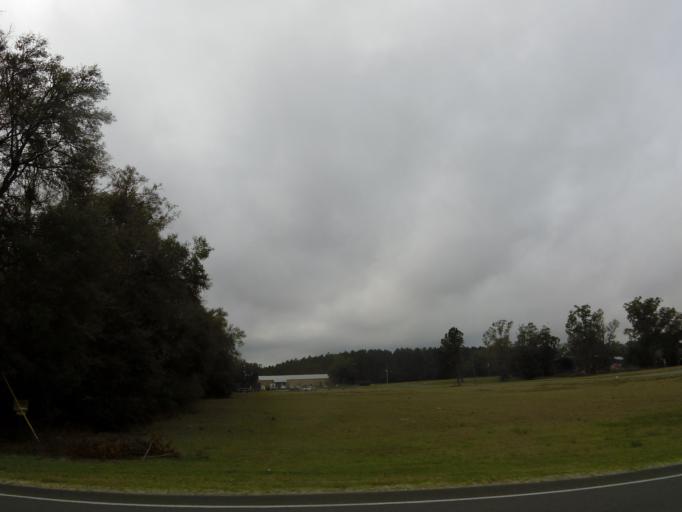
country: US
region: Florida
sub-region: Alachua County
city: High Springs
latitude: 29.8208
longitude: -82.6053
